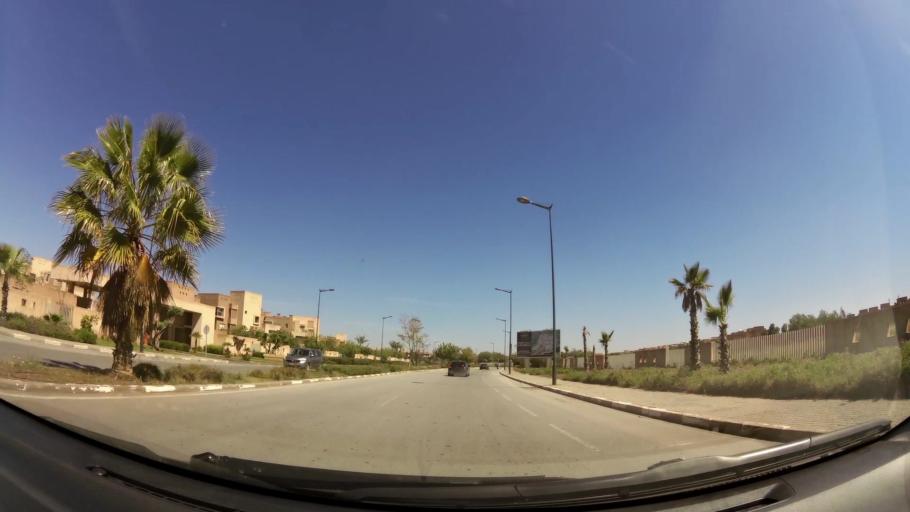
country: MA
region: Marrakech-Tensift-Al Haouz
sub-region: Marrakech
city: Marrakesh
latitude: 31.5982
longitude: -8.0059
